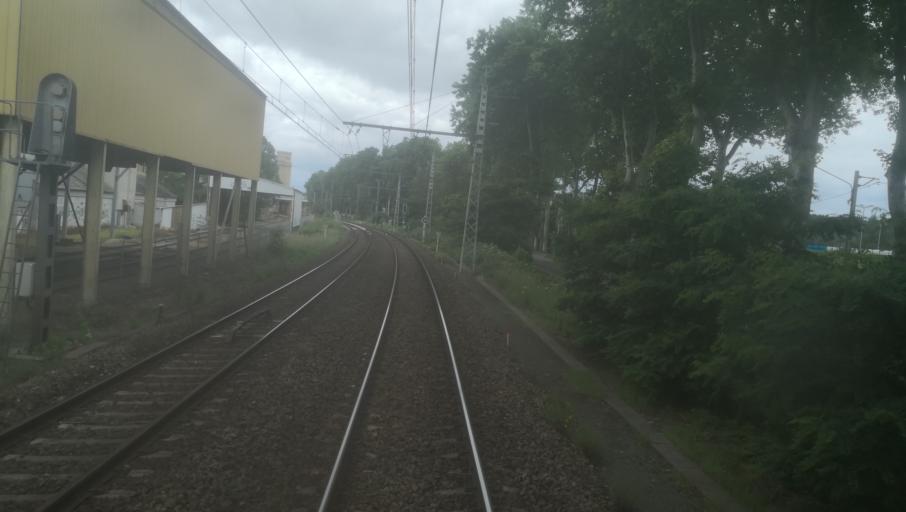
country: FR
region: Midi-Pyrenees
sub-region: Departement de la Haute-Garonne
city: Baziege
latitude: 43.4508
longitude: 1.6276
